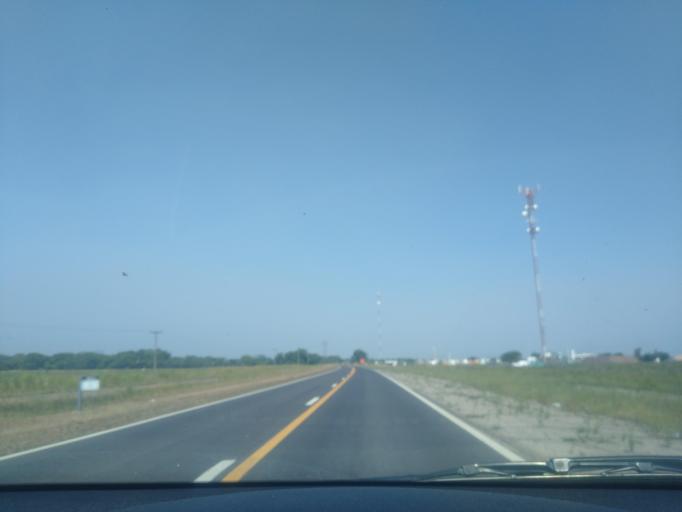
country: AR
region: Chaco
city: Fontana
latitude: -27.5765
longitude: -59.1681
